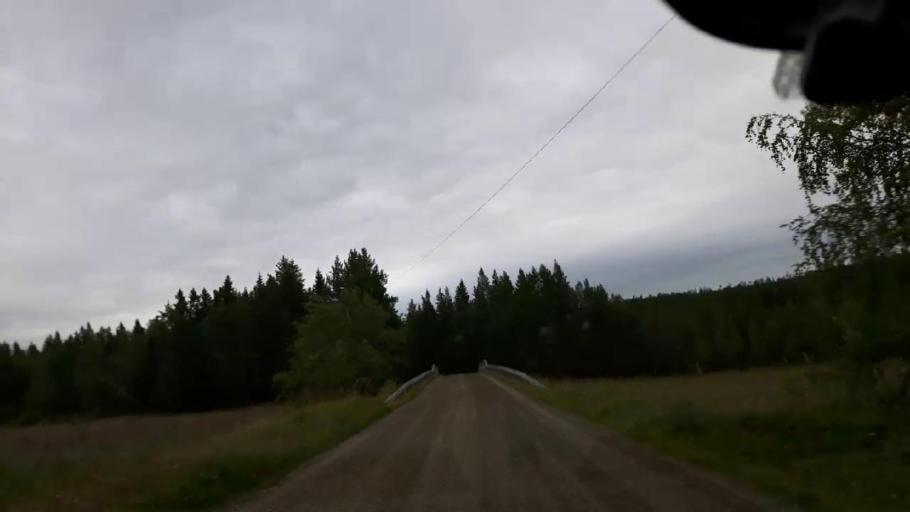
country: SE
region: Jaemtland
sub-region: Braecke Kommun
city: Braecke
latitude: 62.9236
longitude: 15.5426
